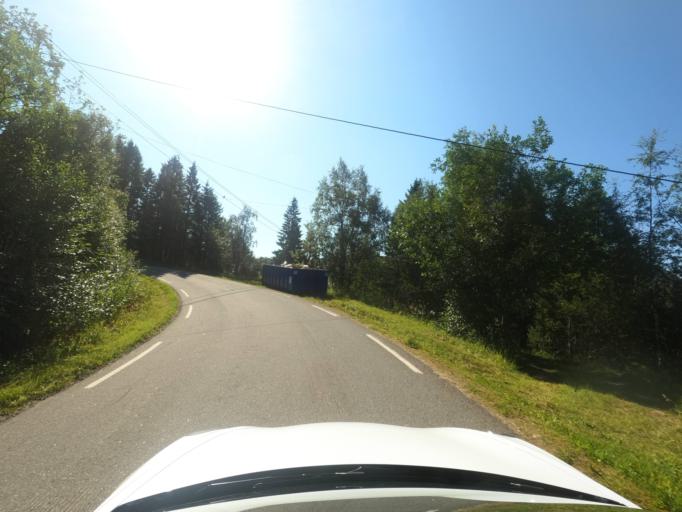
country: NO
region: Nordland
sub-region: Hadsel
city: Stokmarknes
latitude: 68.3050
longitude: 15.0676
